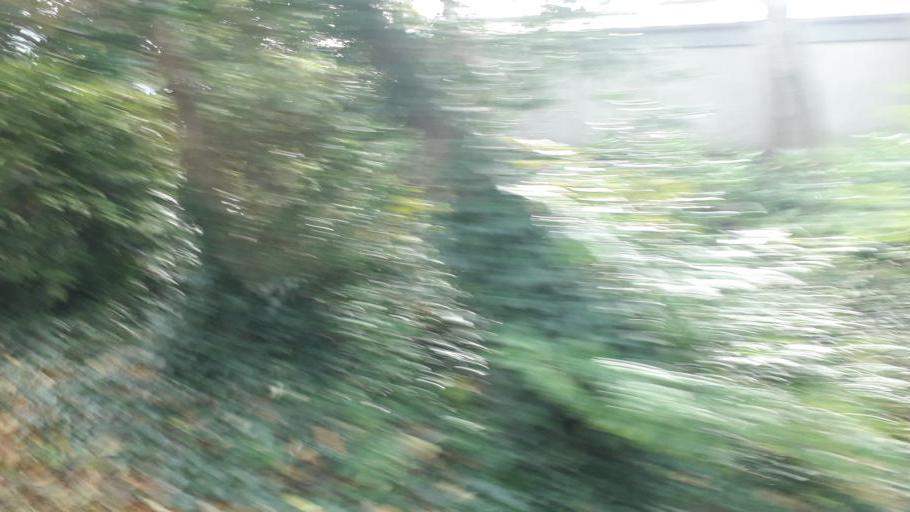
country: IE
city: Clonskeagh
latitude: 53.3091
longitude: -6.2362
